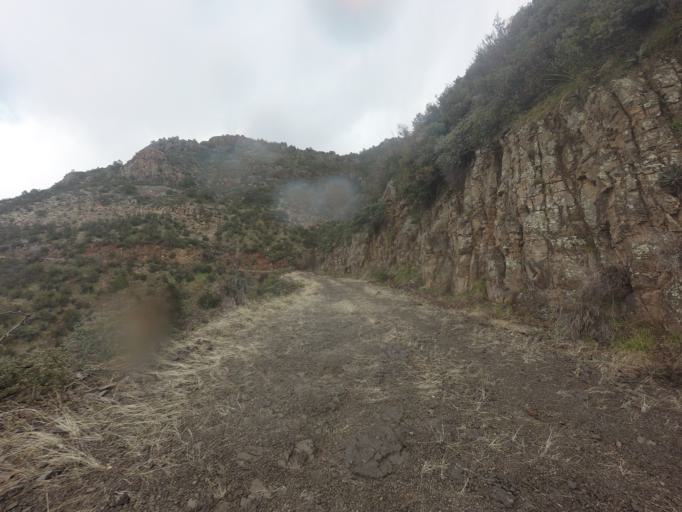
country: US
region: Arizona
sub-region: Gila County
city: Pine
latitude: 34.4038
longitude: -111.5952
